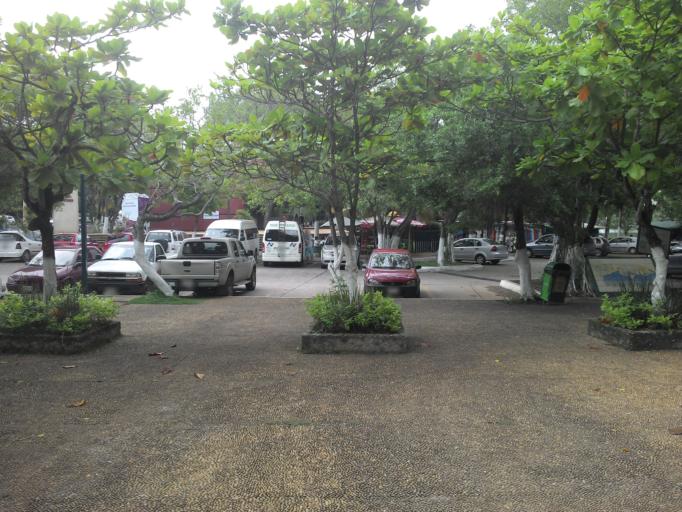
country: MX
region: Tabasco
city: Villahermosa
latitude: 18.0016
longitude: -92.9341
